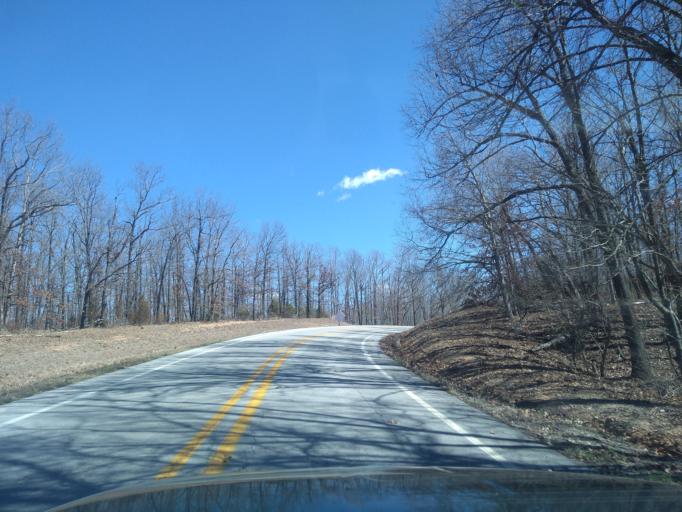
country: US
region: Arkansas
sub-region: Washington County
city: Farmington
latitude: 36.0843
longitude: -94.3238
